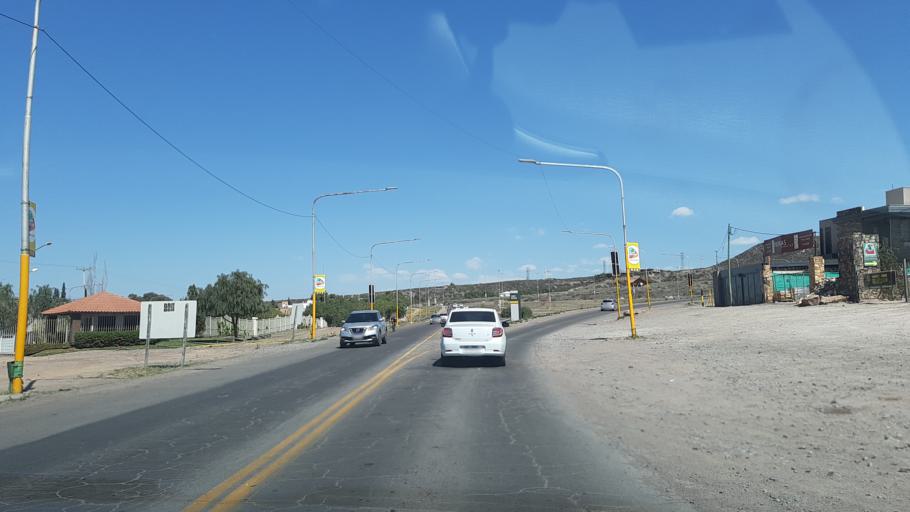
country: AR
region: Mendoza
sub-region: Departamento de Godoy Cruz
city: Godoy Cruz
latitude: -32.9692
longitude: -68.8777
